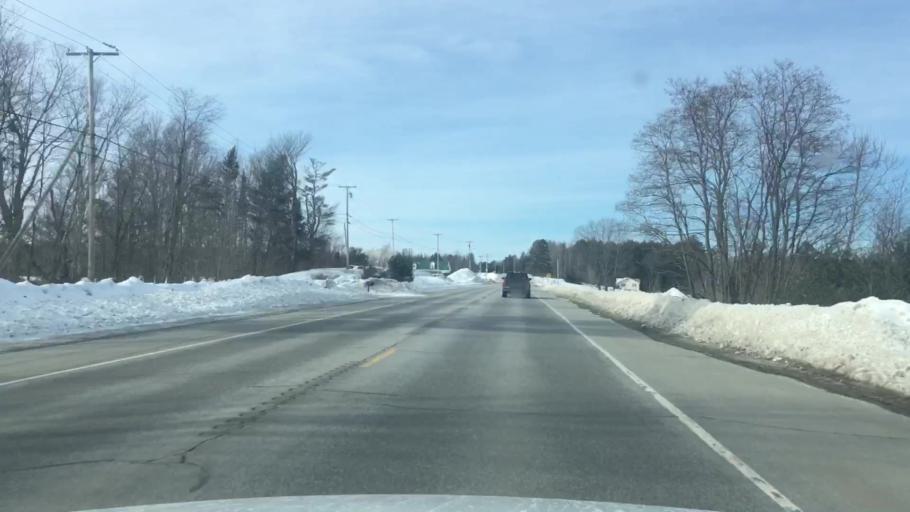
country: US
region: Maine
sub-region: Penobscot County
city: Kenduskeag
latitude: 44.9502
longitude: -68.9475
